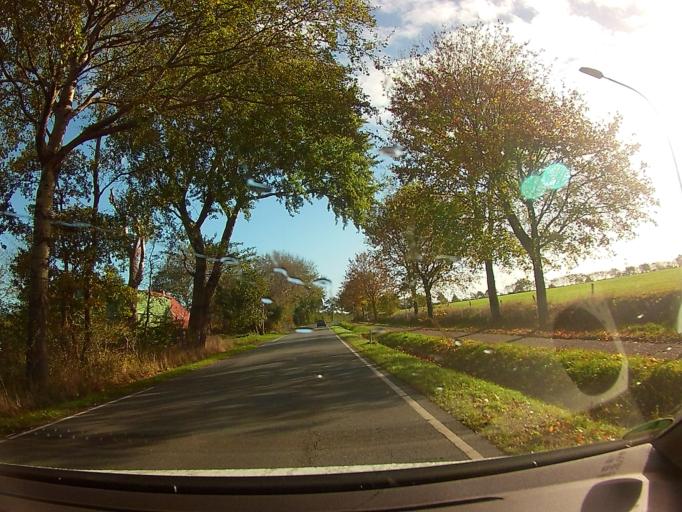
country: DE
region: Schleswig-Holstein
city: Breklum
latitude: 54.6082
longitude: 9.0010
